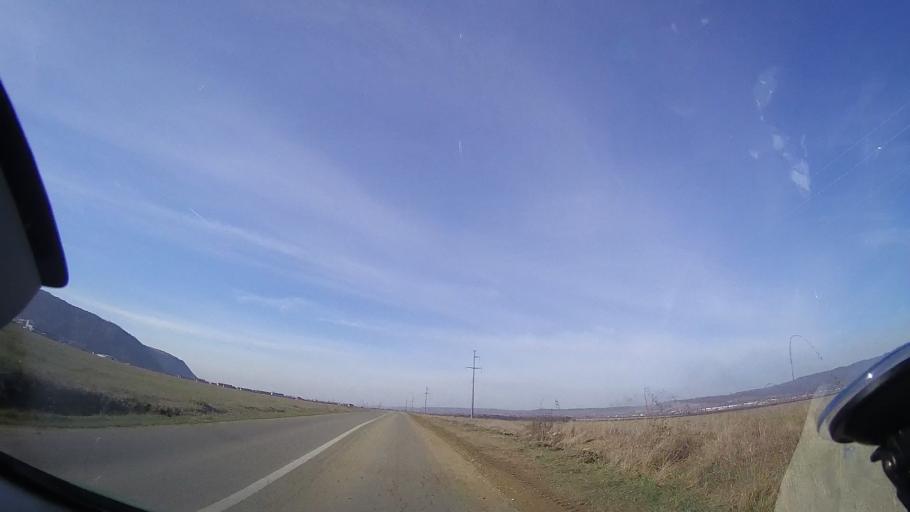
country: RO
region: Bihor
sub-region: Comuna Magesti
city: Magesti
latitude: 47.0211
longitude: 22.4187
